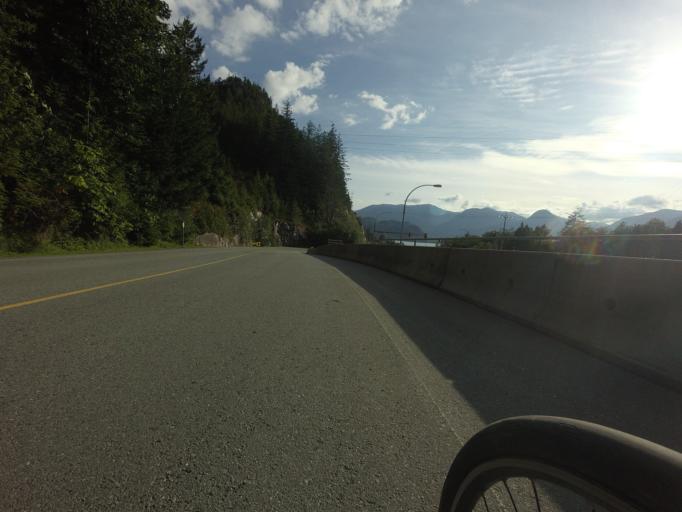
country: CA
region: British Columbia
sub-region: Greater Vancouver Regional District
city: Lions Bay
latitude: 49.6709
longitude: -123.1623
